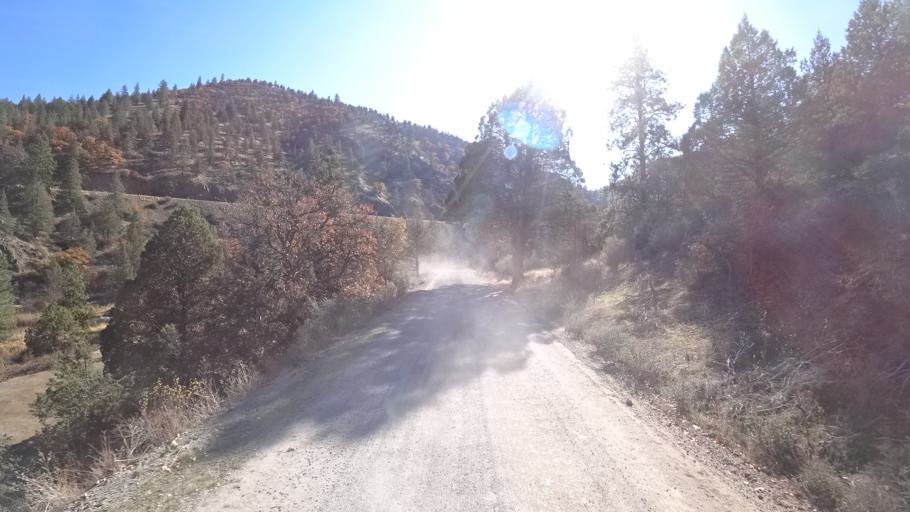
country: US
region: California
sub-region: Siskiyou County
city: Yreka
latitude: 41.7980
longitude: -122.6054
